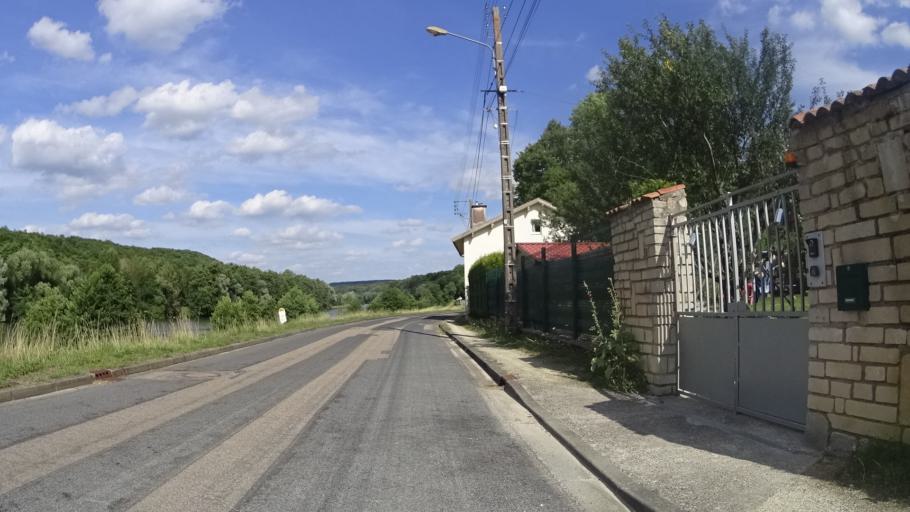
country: FR
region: Lorraine
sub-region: Departement de Meurthe-et-Moselle
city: Dommartin-les-Toul
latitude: 48.6433
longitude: 5.9387
